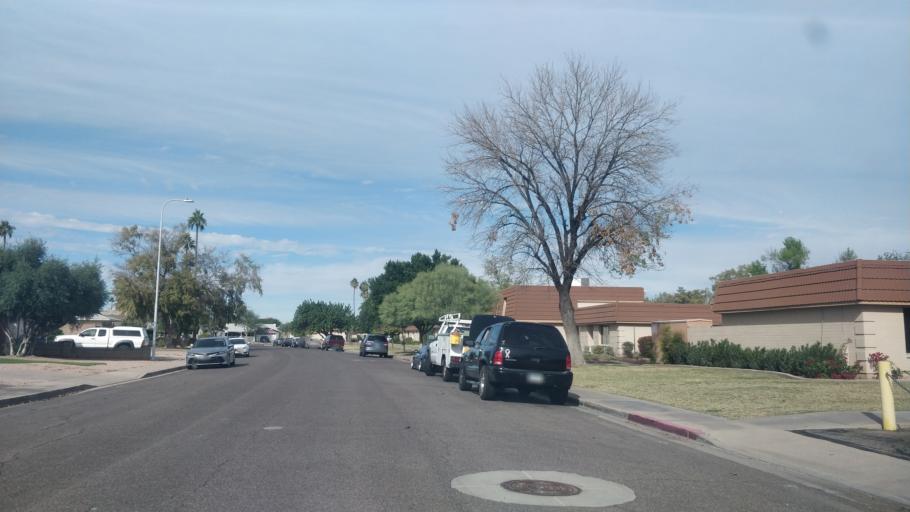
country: US
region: Arizona
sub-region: Maricopa County
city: Tempe
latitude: 33.3797
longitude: -111.9138
